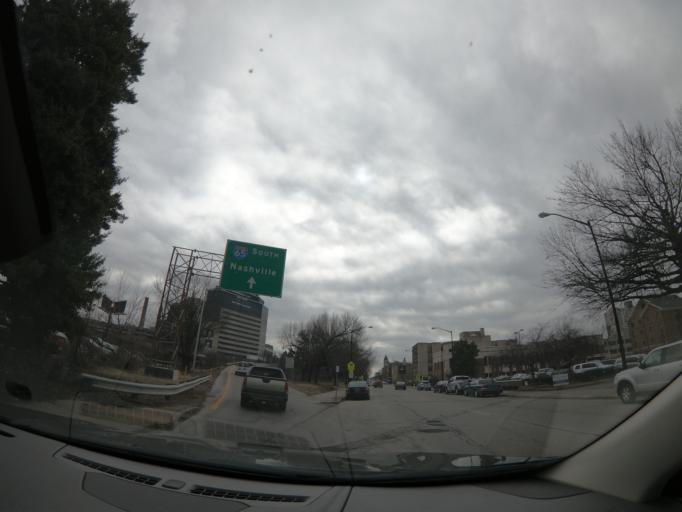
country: US
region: Kentucky
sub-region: Jefferson County
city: Louisville
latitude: 38.2519
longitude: -85.7520
